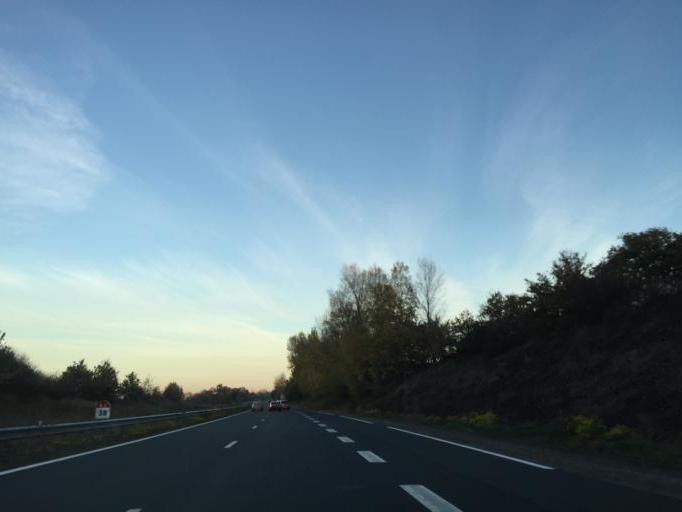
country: FR
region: Rhone-Alpes
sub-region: Departement de la Loire
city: Le Coteau
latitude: 45.9951
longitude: 4.1150
